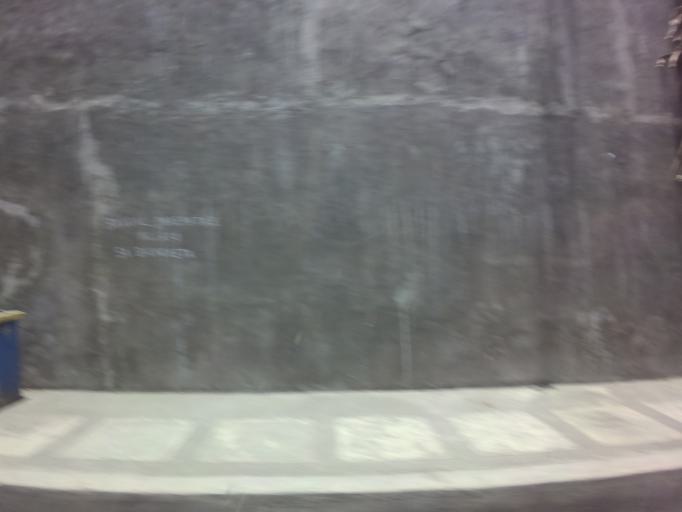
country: PH
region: Metro Manila
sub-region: Marikina
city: Calumpang
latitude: 14.6058
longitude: 121.1042
